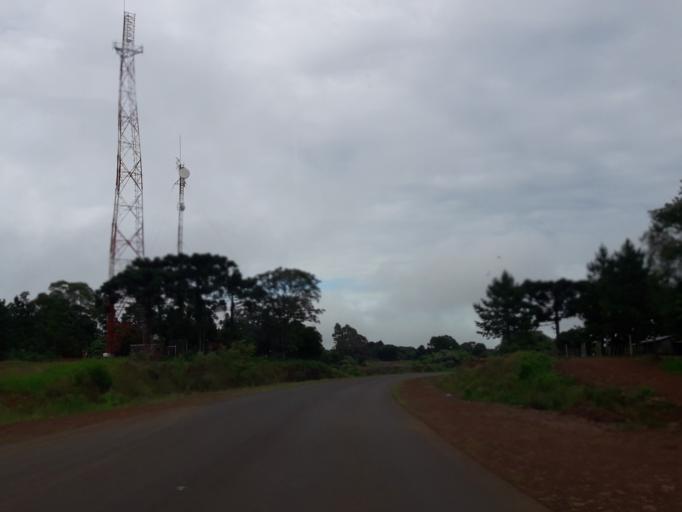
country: AR
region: Misiones
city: Bernardo de Irigoyen
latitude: -26.4253
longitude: -53.8414
